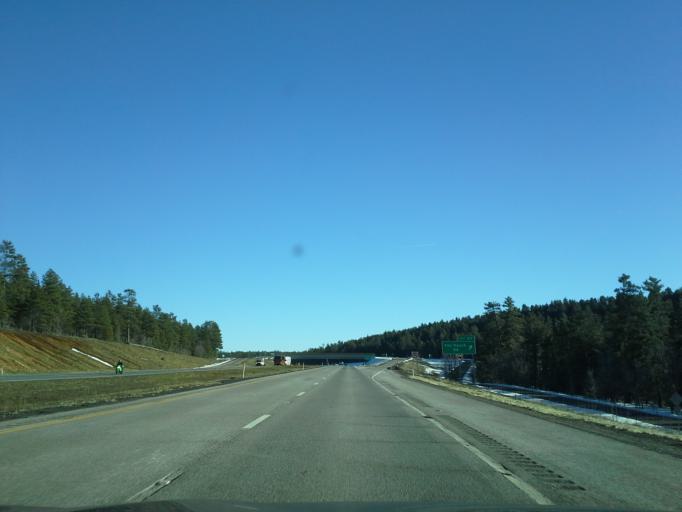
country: US
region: Arizona
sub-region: Coconino County
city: Sedona
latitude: 34.8792
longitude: -111.6378
